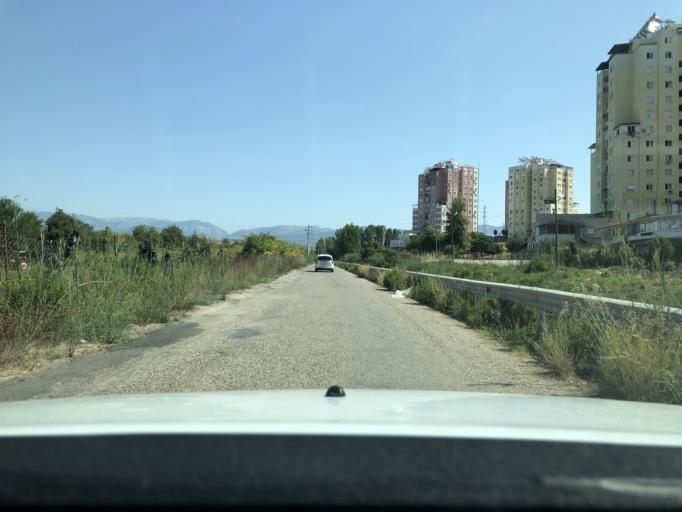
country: TR
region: Antalya
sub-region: Manavgat
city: Manavgat
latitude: 36.7956
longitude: 31.4635
